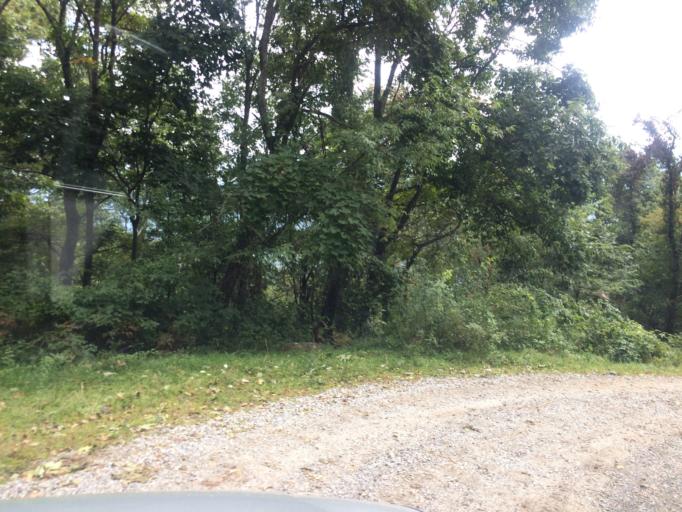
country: US
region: North Carolina
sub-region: Haywood County
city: Clyde
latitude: 35.5635
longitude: -82.9109
